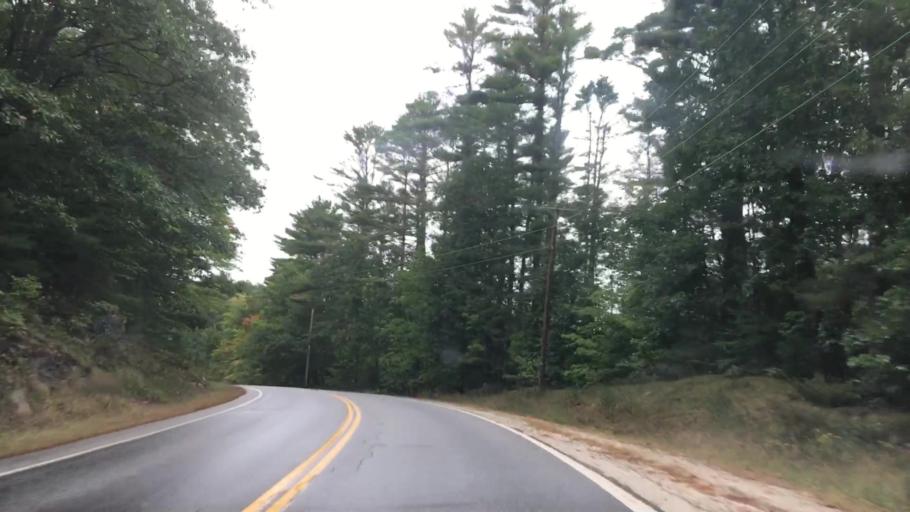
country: US
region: Maine
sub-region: Cumberland County
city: Raymond
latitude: 43.9635
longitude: -70.4650
